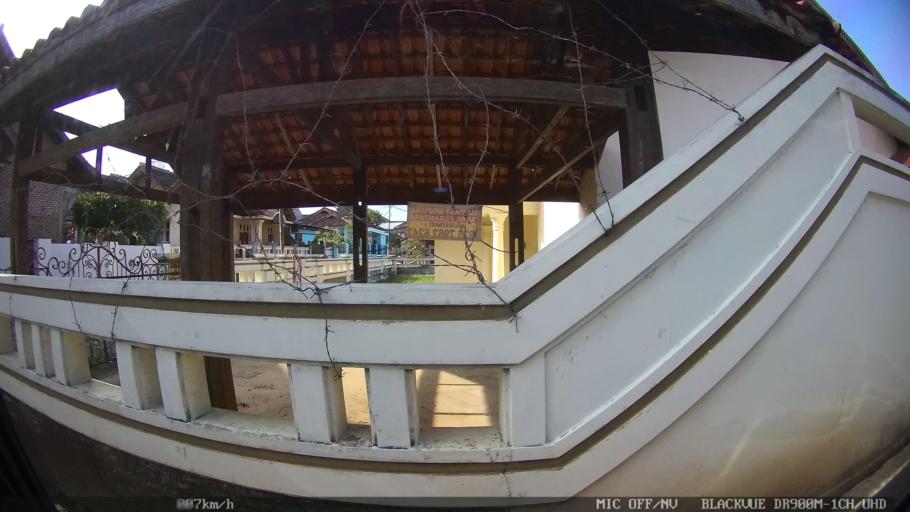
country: ID
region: Lampung
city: Kedaton
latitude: -5.3758
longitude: 105.2348
